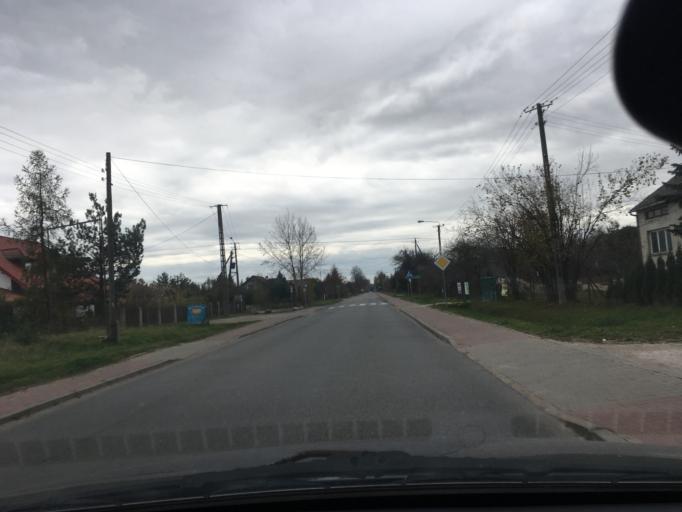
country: PL
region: Lodz Voivodeship
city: Zabia Wola
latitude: 52.0299
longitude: 20.6908
